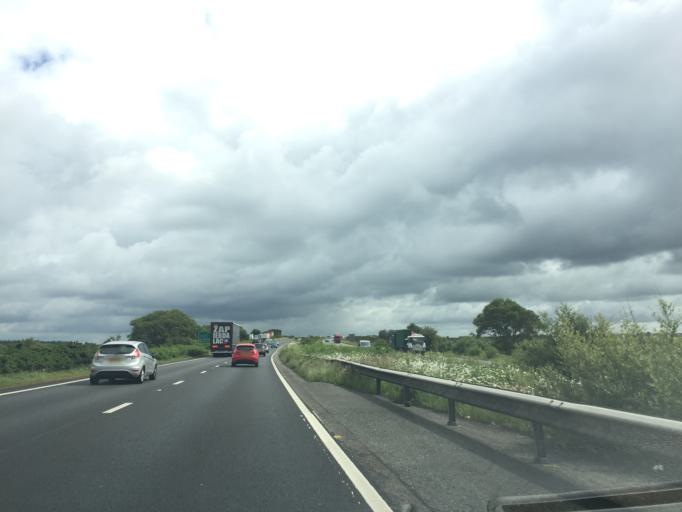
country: GB
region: England
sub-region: Hampshire
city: Ringwood
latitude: 50.8599
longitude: -1.7207
